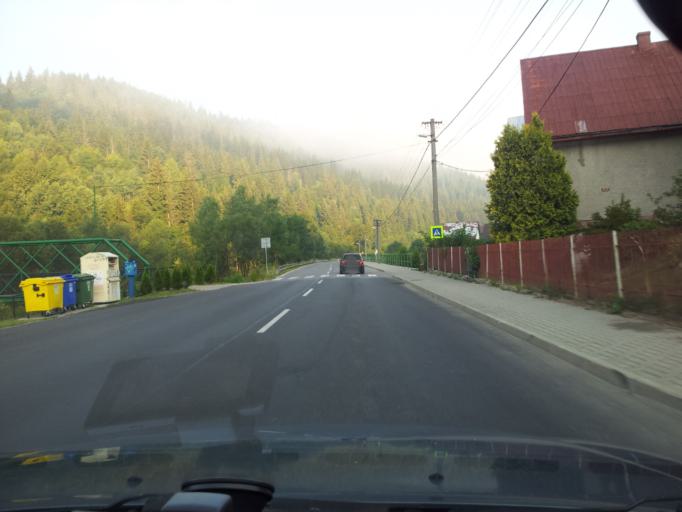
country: SK
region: Zilinsky
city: Cadca
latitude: 49.3700
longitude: 18.9000
